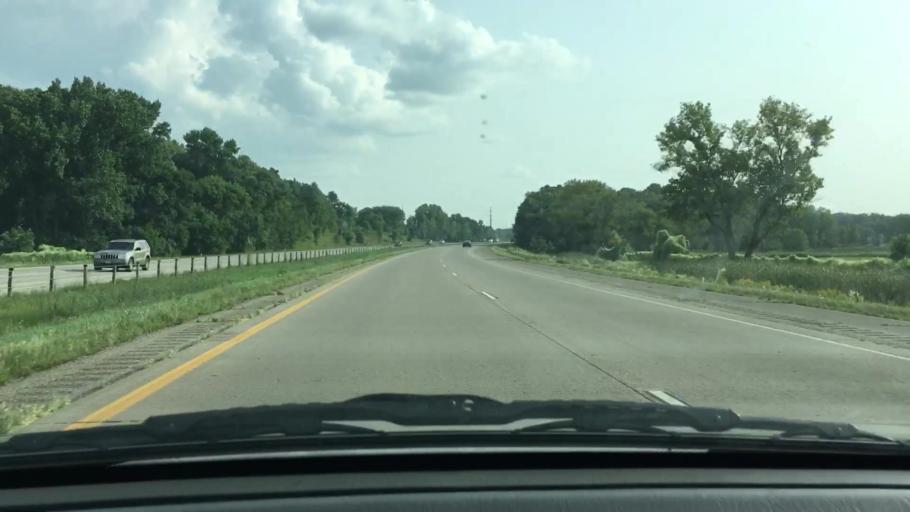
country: US
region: Minnesota
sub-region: Scott County
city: Elko New Market
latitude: 44.6085
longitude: -93.2961
